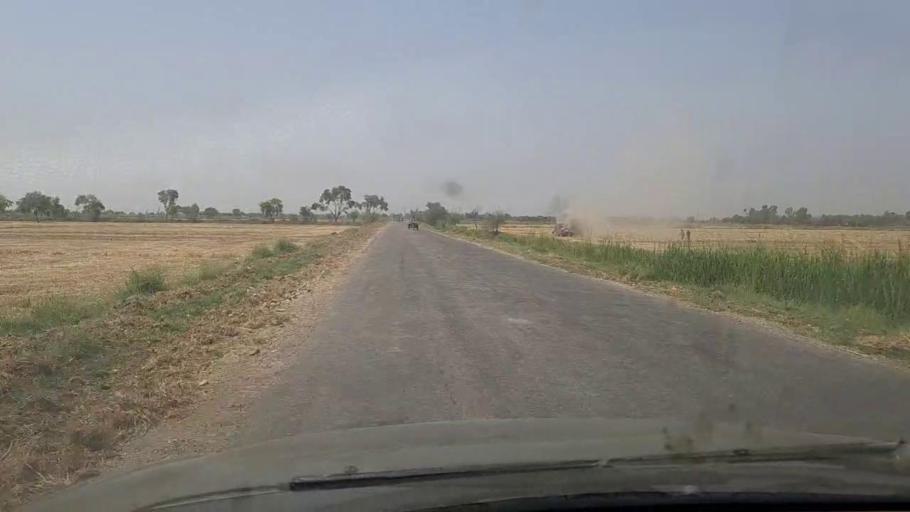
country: PK
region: Sindh
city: Khanpur
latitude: 27.8585
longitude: 69.4334
